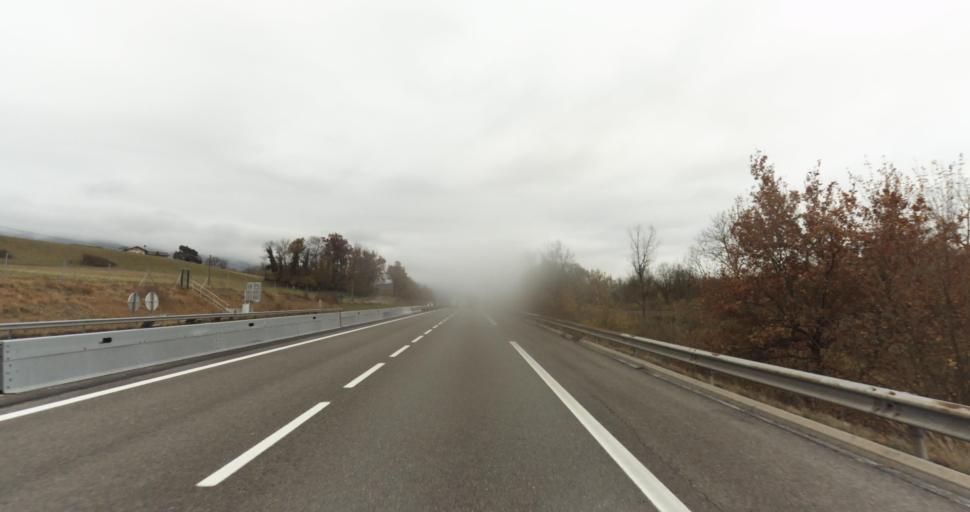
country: FR
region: Rhone-Alpes
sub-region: Departement de la Haute-Savoie
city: Chavanod
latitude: 45.8531
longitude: 6.0564
